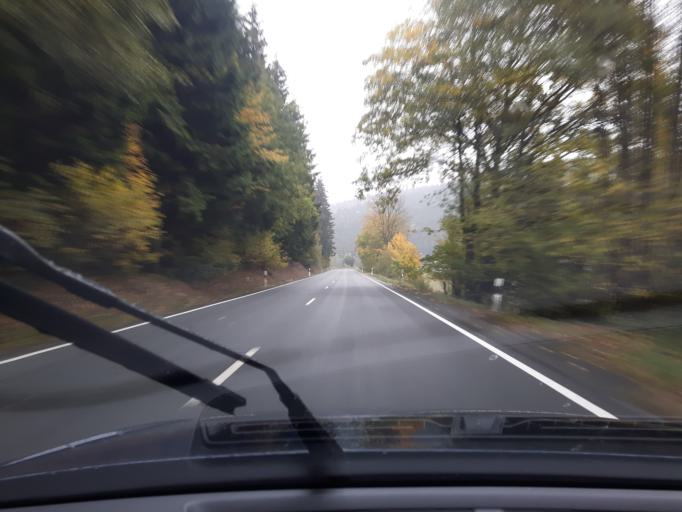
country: DE
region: North Rhine-Westphalia
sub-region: Regierungsbezirk Arnsberg
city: Bad Berleburg
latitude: 51.0025
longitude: 8.4044
